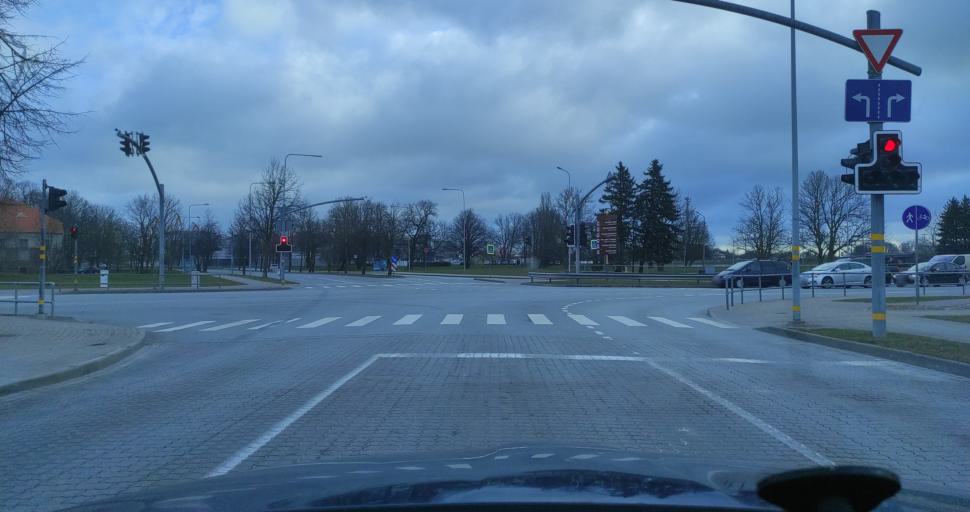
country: LV
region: Ventspils
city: Ventspils
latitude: 57.3876
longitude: 21.5822
